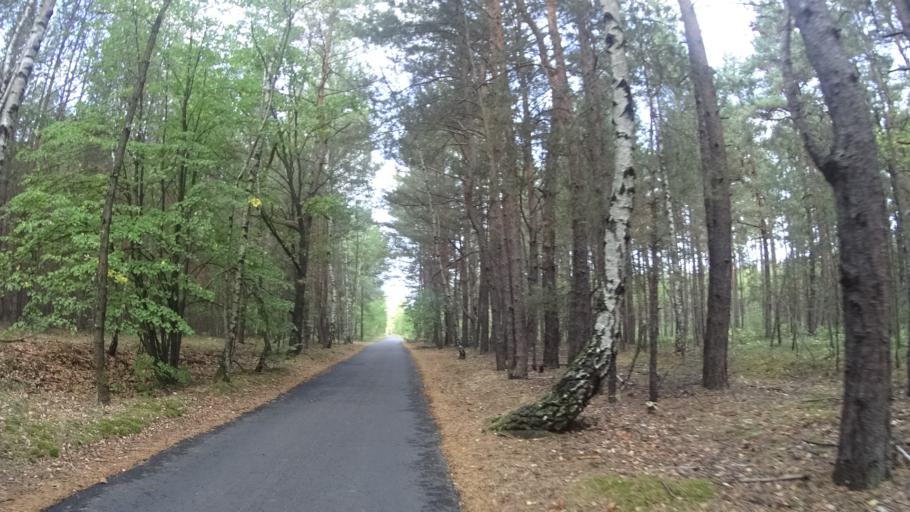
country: DE
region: Brandenburg
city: Tschernitz
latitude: 51.5862
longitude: 14.6031
